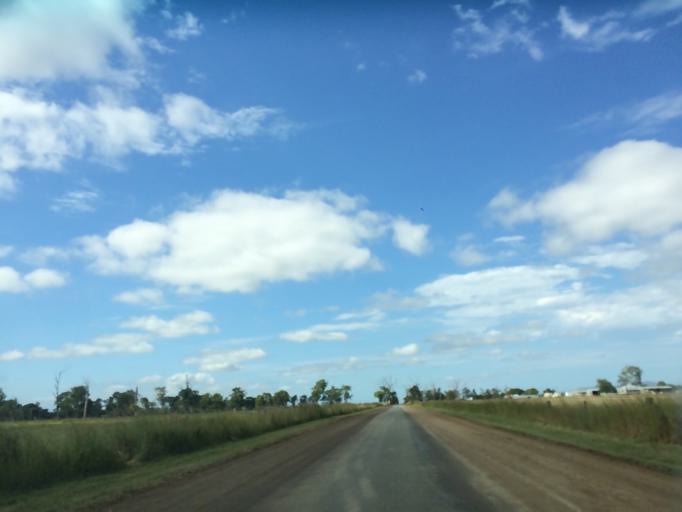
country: AU
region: Queensland
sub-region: Logan
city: Cedar Vale
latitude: -27.8744
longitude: 152.9563
